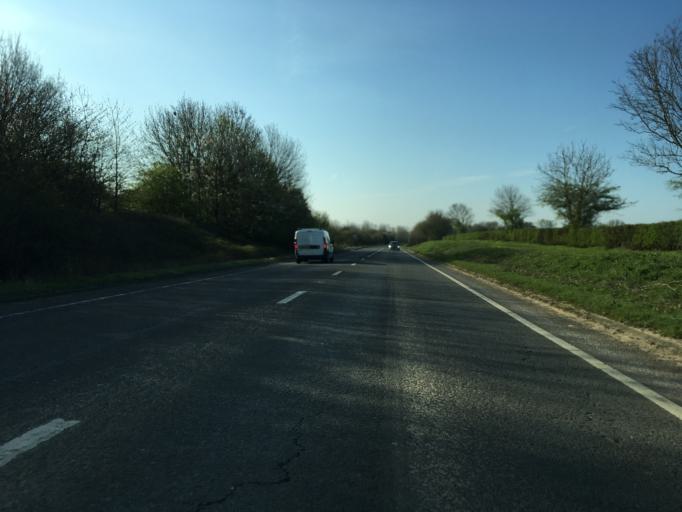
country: GB
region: England
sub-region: Milton Keynes
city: Stony Stratford
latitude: 52.0593
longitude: -0.8708
